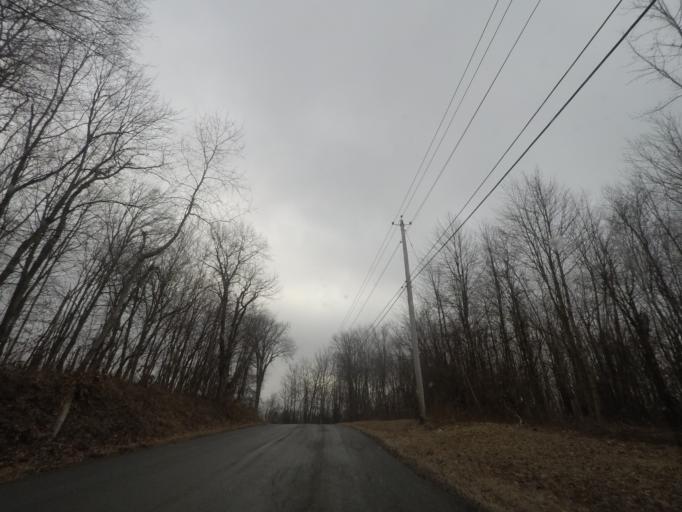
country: US
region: New York
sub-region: Saratoga County
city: Waterford
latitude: 42.7696
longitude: -73.6570
